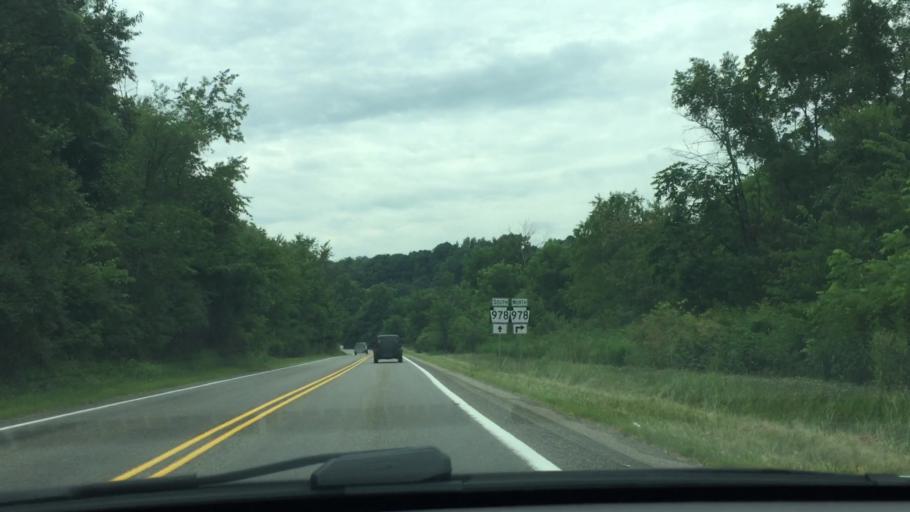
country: US
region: Pennsylvania
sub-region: Allegheny County
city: Oakdale
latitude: 40.4118
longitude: -80.1913
